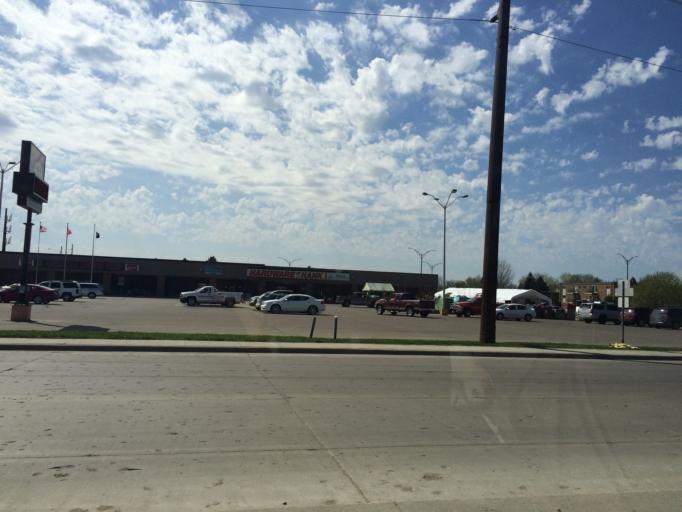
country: US
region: Minnesota
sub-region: Polk County
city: East Grand Forks
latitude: 47.9349
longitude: -97.0201
